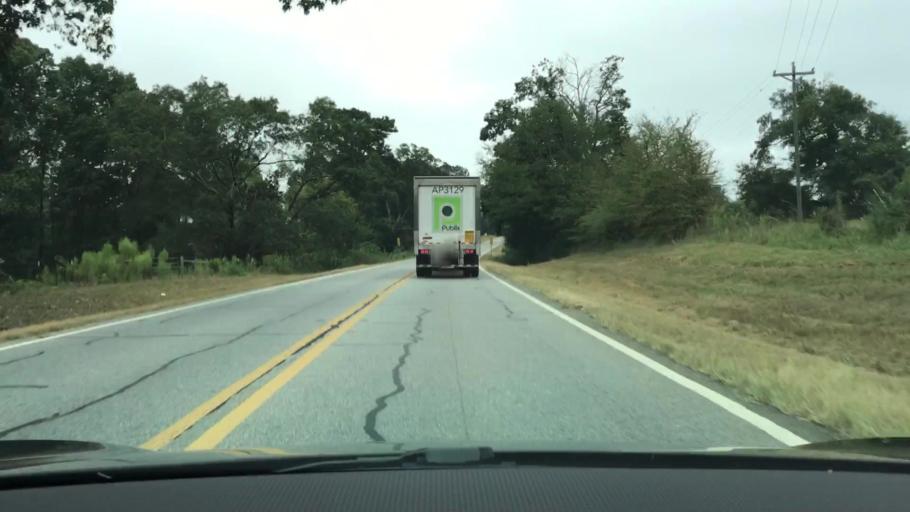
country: US
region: Georgia
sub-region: Oconee County
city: Watkinsville
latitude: 33.7401
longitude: -83.3033
